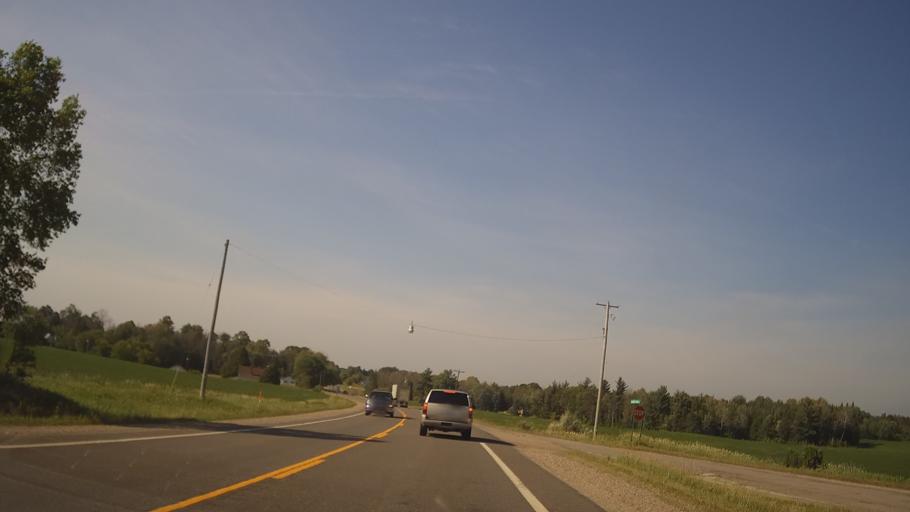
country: US
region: Michigan
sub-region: Ogemaw County
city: West Branch
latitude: 44.3705
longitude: -84.1161
